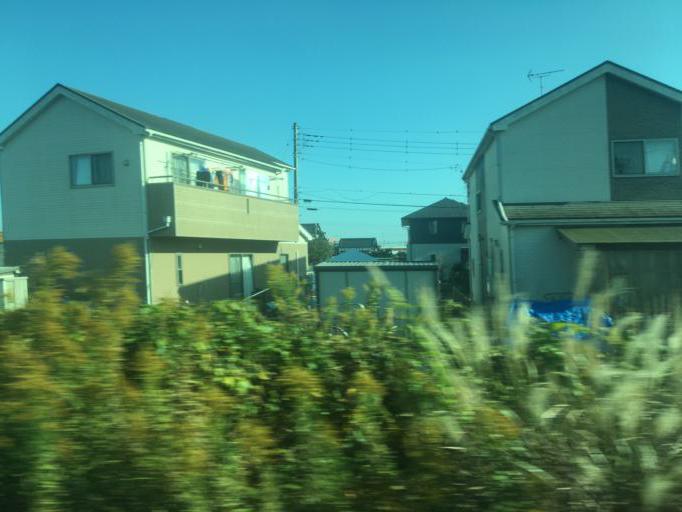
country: JP
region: Ibaraki
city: Naka
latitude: 36.0378
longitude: 140.1714
